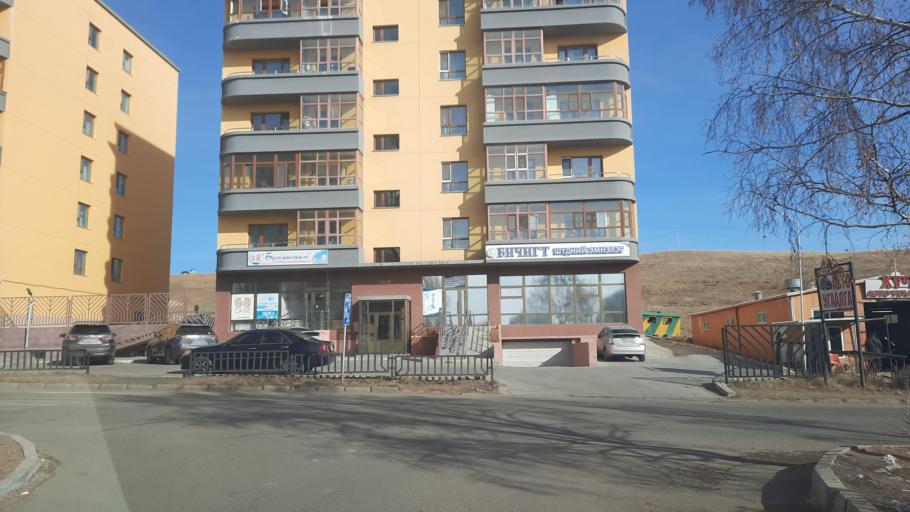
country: MN
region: Orhon
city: Erdenet
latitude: 49.0350
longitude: 104.0582
